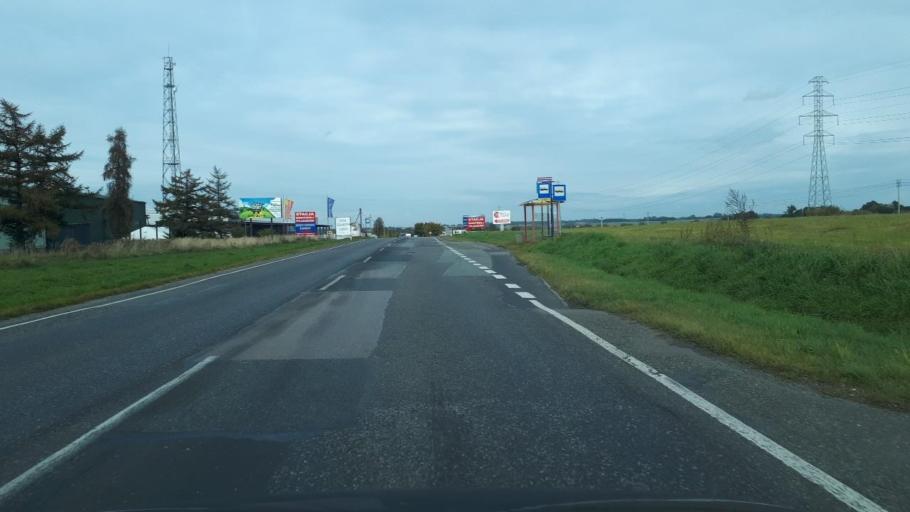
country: PL
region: Silesian Voivodeship
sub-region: Powiat gliwicki
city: Pyskowice
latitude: 50.3831
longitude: 18.6347
